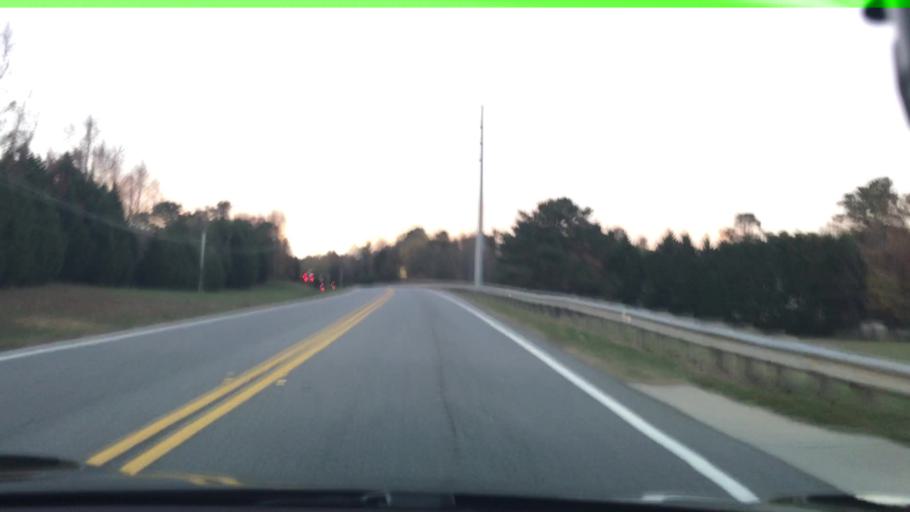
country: US
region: Georgia
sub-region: Gwinnett County
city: Suwanee
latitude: 34.0901
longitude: -84.1336
